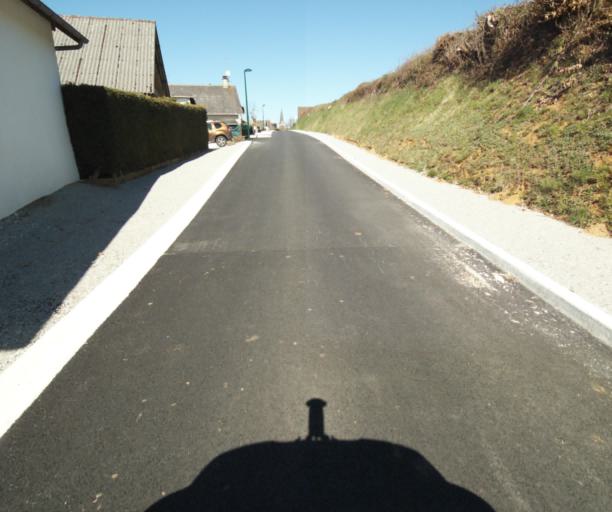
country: FR
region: Limousin
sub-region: Departement de la Correze
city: Seilhac
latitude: 45.3631
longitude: 1.7158
